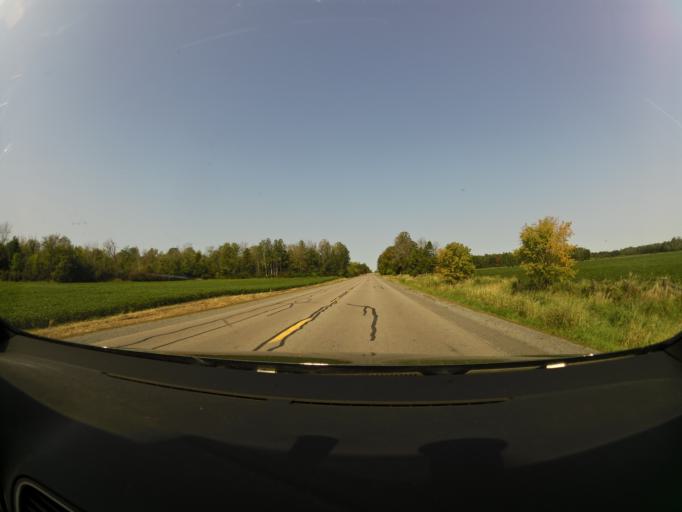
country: CA
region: Ontario
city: Arnprior
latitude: 45.4212
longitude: -76.1557
